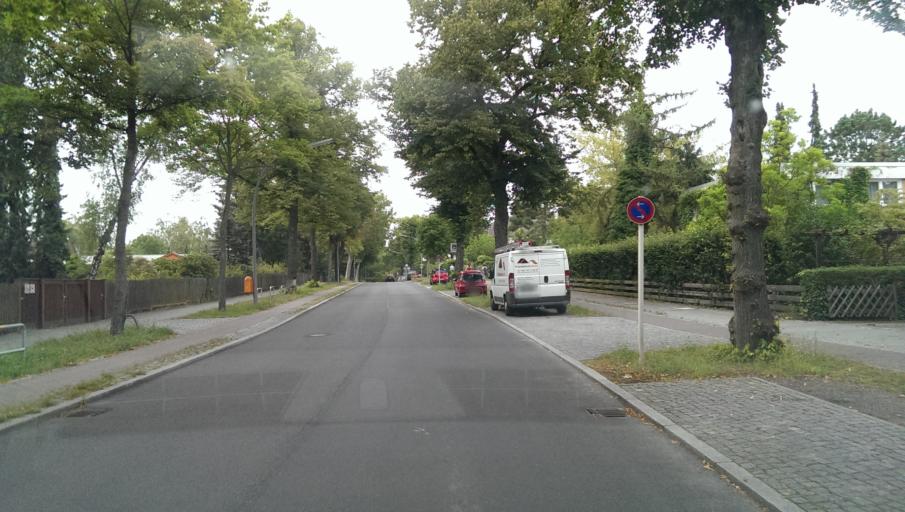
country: DE
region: Berlin
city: Zehlendorf Bezirk
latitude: 52.4382
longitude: 13.2567
